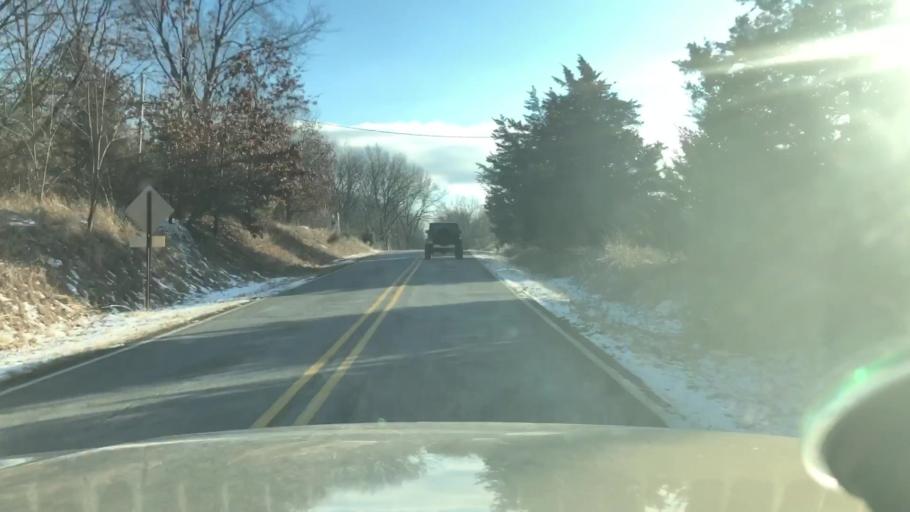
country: US
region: Michigan
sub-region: Jackson County
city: Vandercook Lake
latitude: 42.1151
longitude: -84.4514
